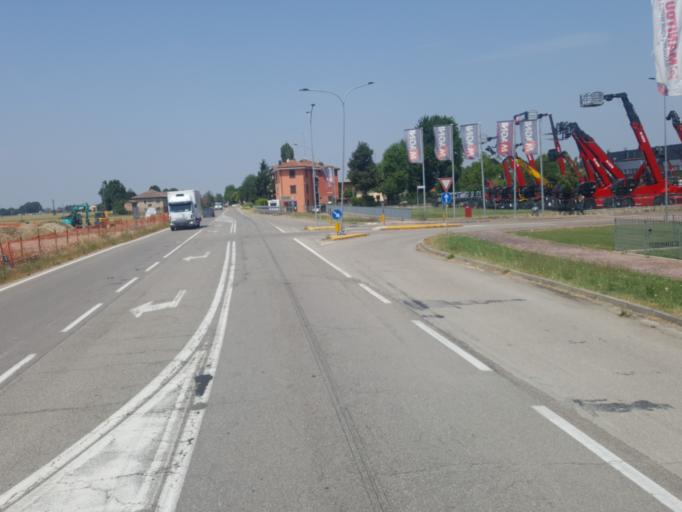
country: IT
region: Emilia-Romagna
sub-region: Provincia di Modena
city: Cavazzona
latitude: 44.5706
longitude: 11.1228
